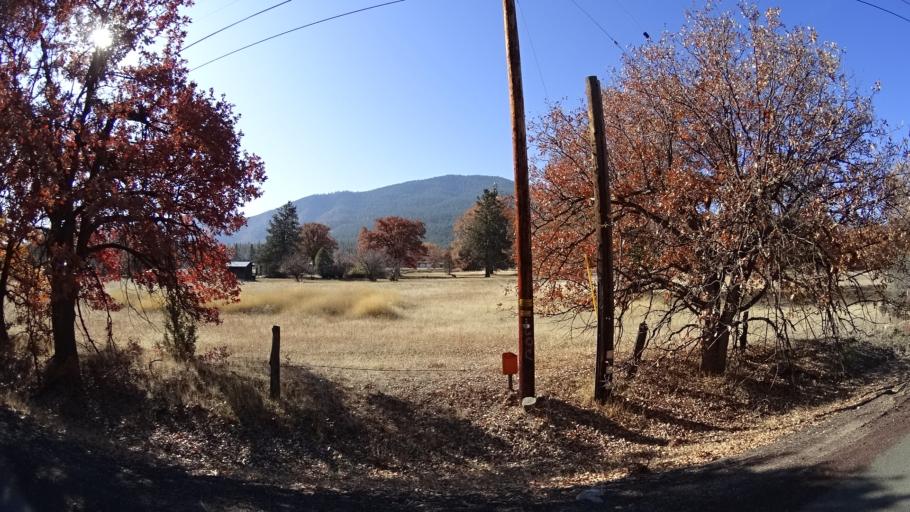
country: US
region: California
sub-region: Siskiyou County
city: Yreka
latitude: 41.6605
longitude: -122.5974
